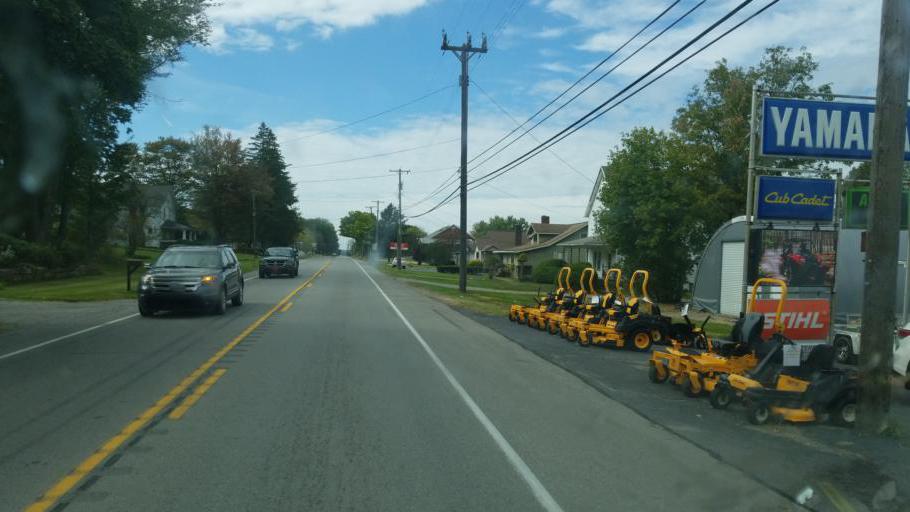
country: US
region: Pennsylvania
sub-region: Mercer County
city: Greenville
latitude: 41.4170
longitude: -80.3387
